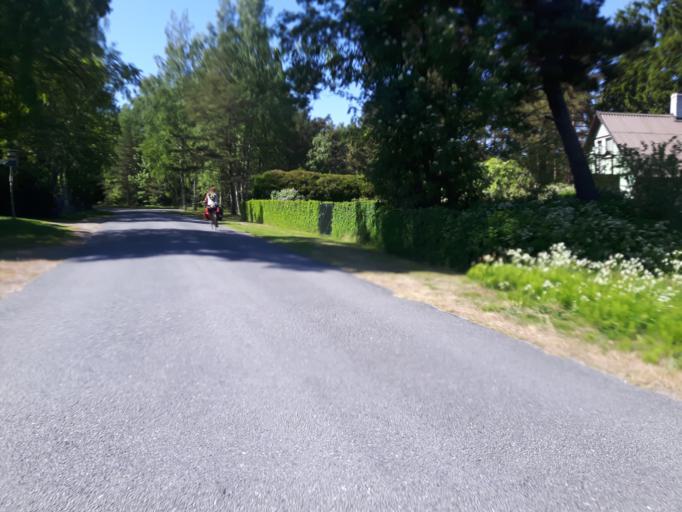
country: EE
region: Laeaene-Virumaa
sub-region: Haljala vald
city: Haljala
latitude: 59.5767
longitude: 26.2722
